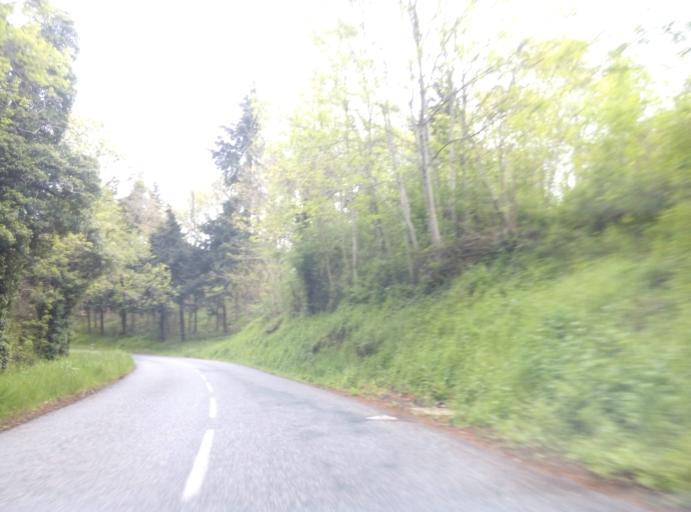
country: FR
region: Rhone-Alpes
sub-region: Departement du Rhone
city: Tarare
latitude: 45.9220
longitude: 4.4293
